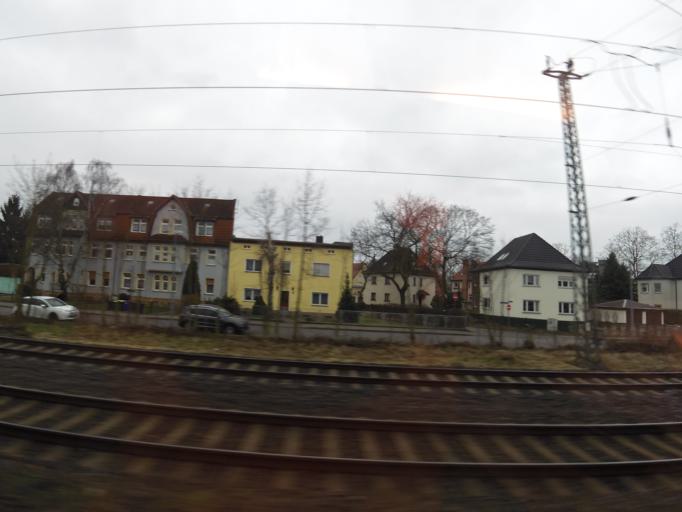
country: DE
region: Saxony-Anhalt
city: Schonebeck
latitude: 52.0153
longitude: 11.7393
